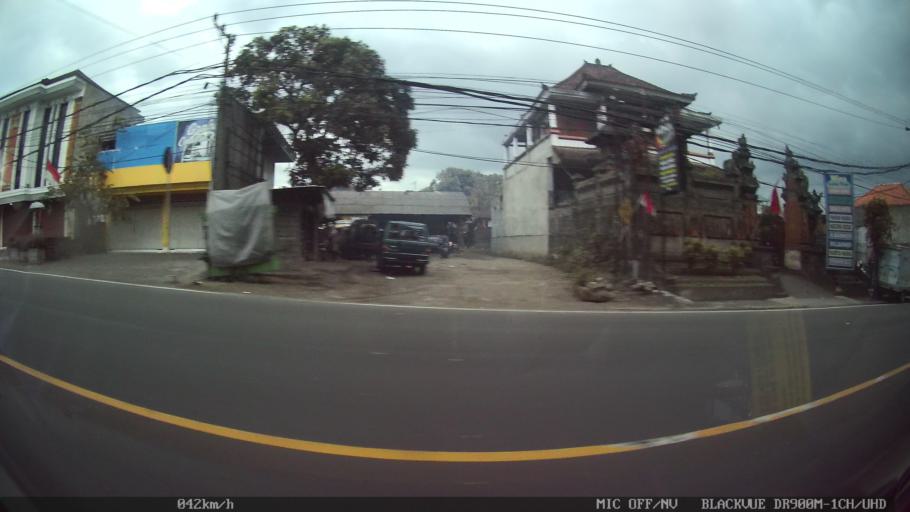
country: ID
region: Bali
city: Banjar Tegal Belodan
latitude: -8.5449
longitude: 115.1143
